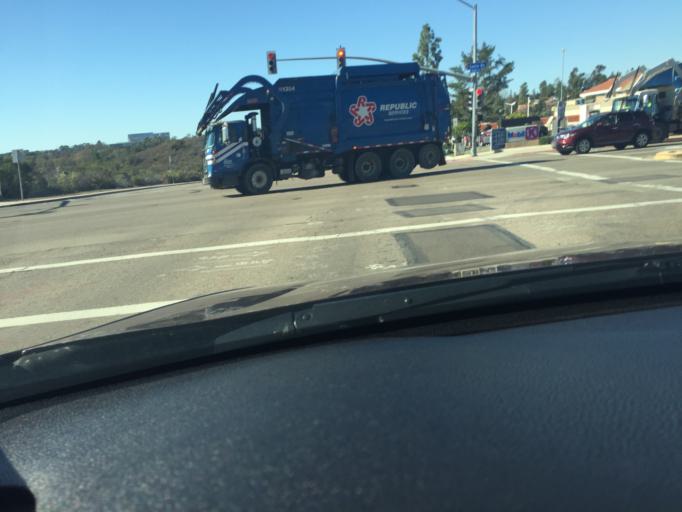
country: US
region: California
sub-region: San Diego County
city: La Mesa
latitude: 32.8293
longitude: -117.1031
